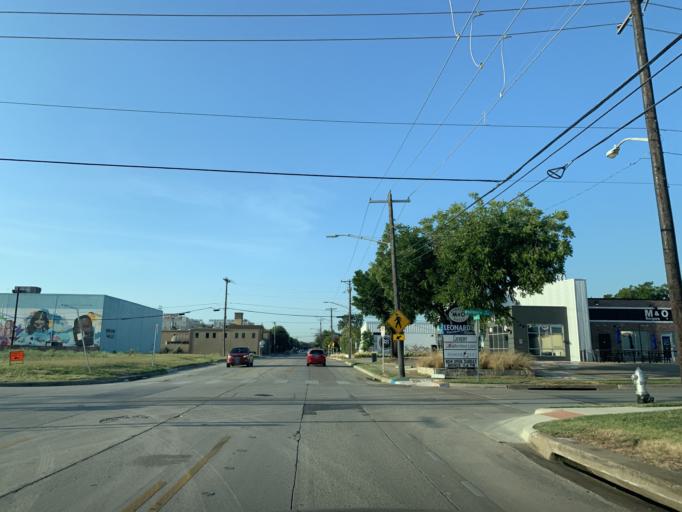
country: US
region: Texas
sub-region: Tarrant County
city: River Oaks
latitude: 32.7583
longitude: -97.3547
